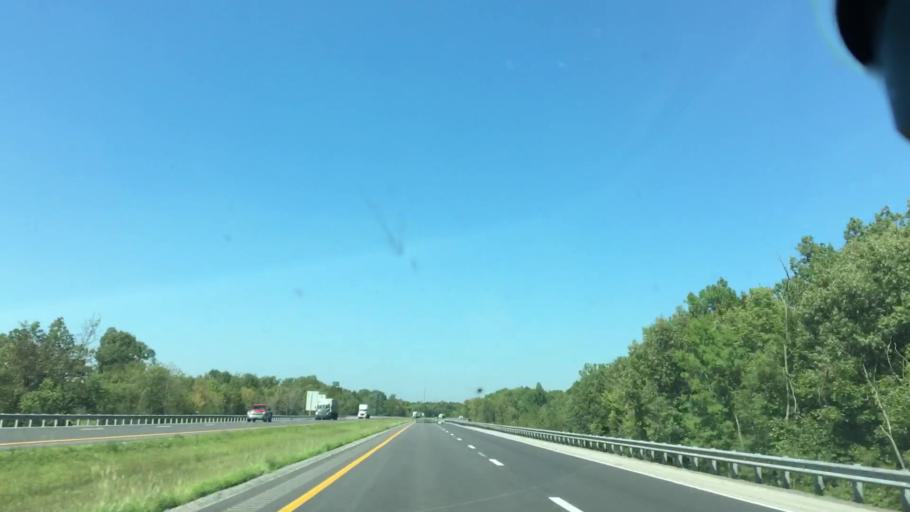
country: US
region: Kentucky
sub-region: Webster County
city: Sebree
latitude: 37.6196
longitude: -87.5036
